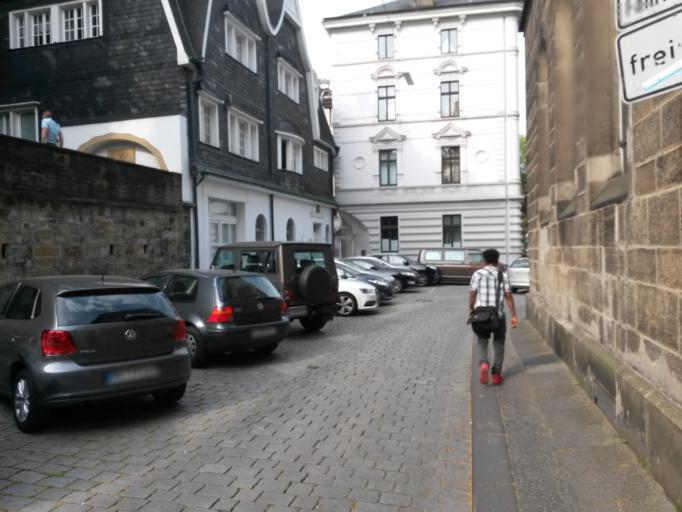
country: DE
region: North Rhine-Westphalia
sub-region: Regierungsbezirk Dusseldorf
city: Wuppertal
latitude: 51.2553
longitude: 7.1347
